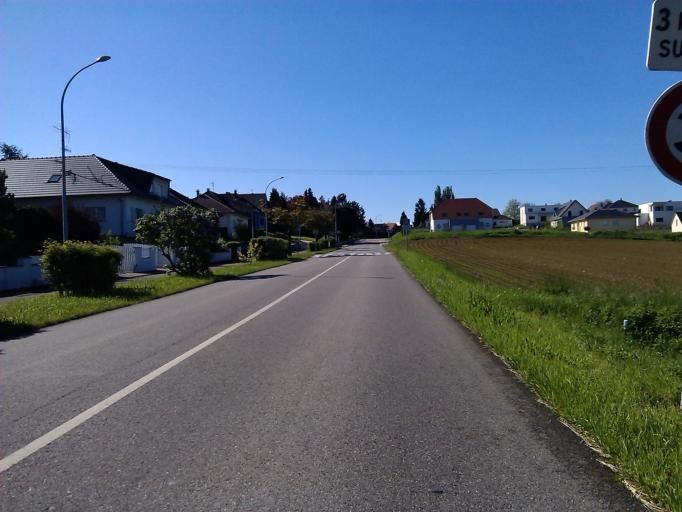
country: FR
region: Alsace
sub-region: Departement du Haut-Rhin
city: Heimsbrunn
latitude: 47.7100
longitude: 7.2252
